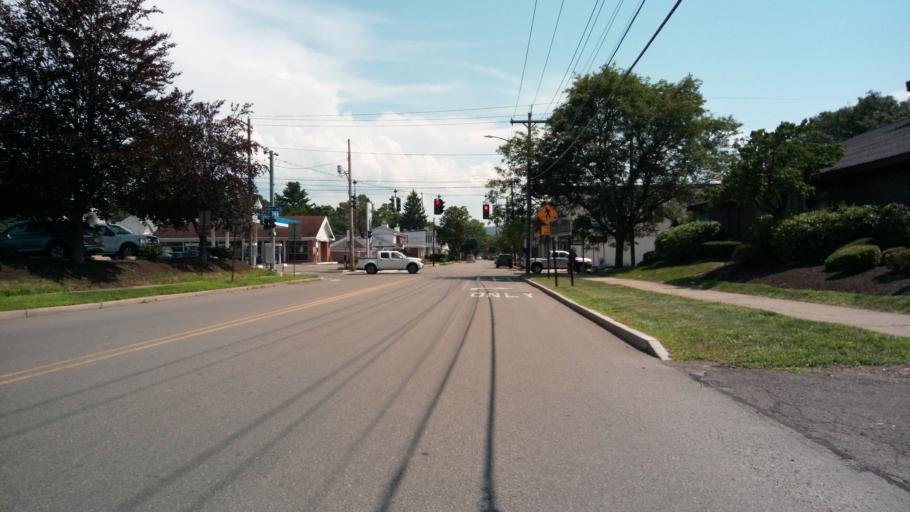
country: US
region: New York
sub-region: Chemung County
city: Elmira
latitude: 42.0860
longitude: -76.8232
